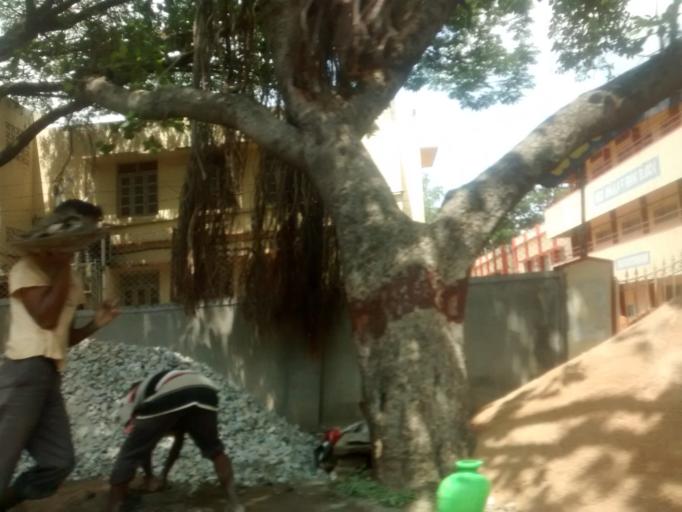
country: IN
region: Karnataka
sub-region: Mysore
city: Mysore
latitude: 12.3078
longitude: 76.6441
